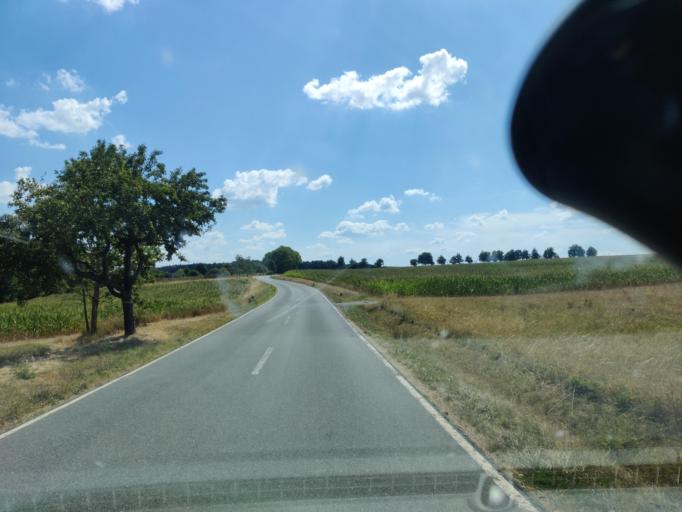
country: DE
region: Bavaria
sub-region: Regierungsbezirk Mittelfranken
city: Thalmassing
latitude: 49.0755
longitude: 11.1928
